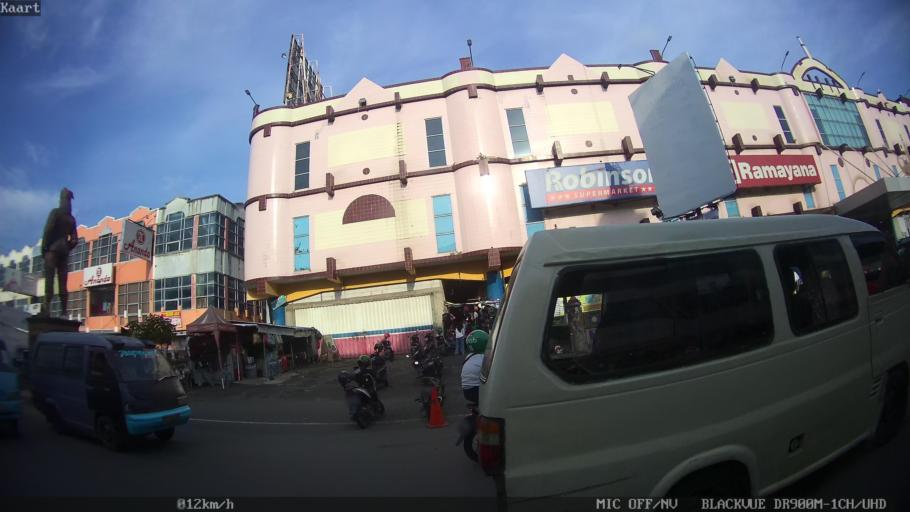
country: ID
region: Lampung
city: Bandarlampung
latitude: -5.4101
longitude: 105.2586
